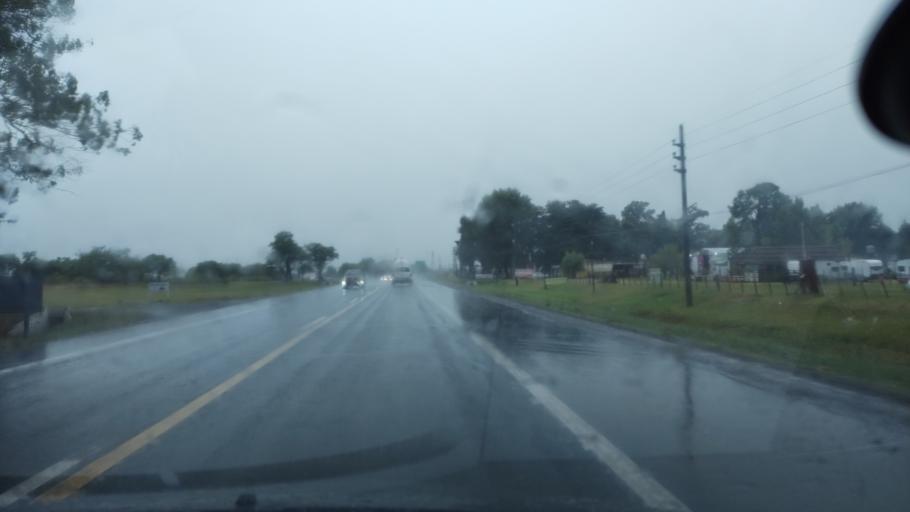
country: AR
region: Buenos Aires
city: Canuelas
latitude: -35.0291
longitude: -58.7482
